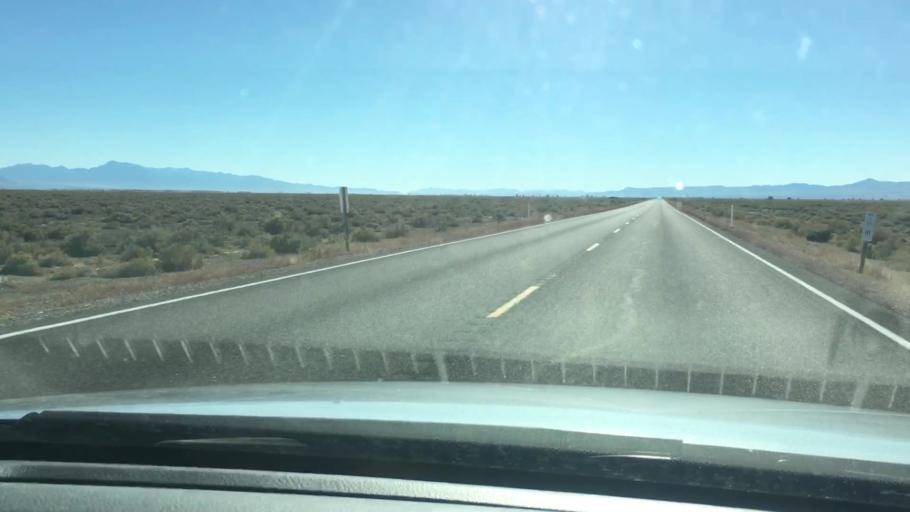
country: US
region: Nevada
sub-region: White Pine County
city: Ely
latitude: 38.6678
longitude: -115.5612
